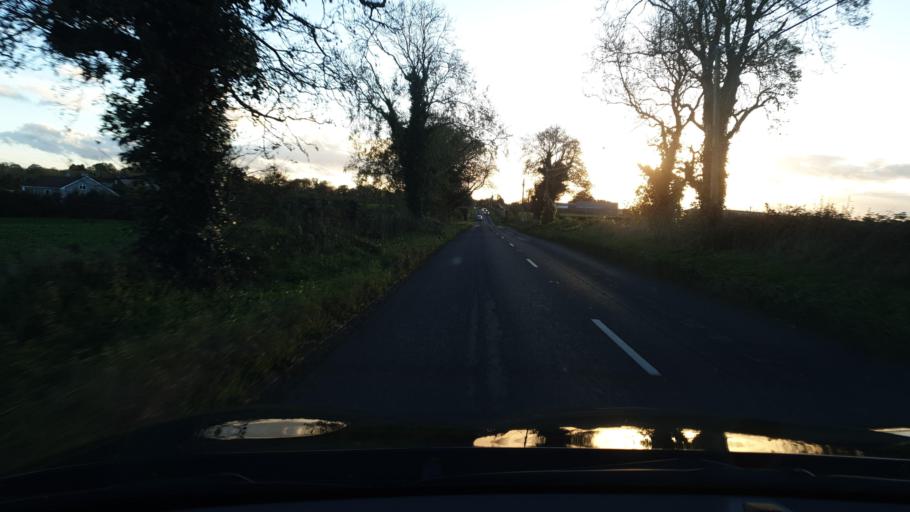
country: IE
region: Leinster
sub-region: Lu
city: Termonfeckin
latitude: 53.7494
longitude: -6.2876
